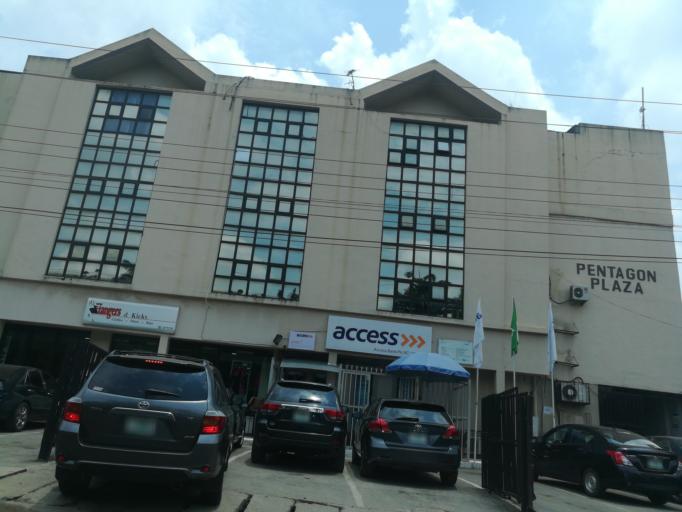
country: NG
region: Lagos
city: Ikeja
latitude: 6.5933
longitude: 3.3579
